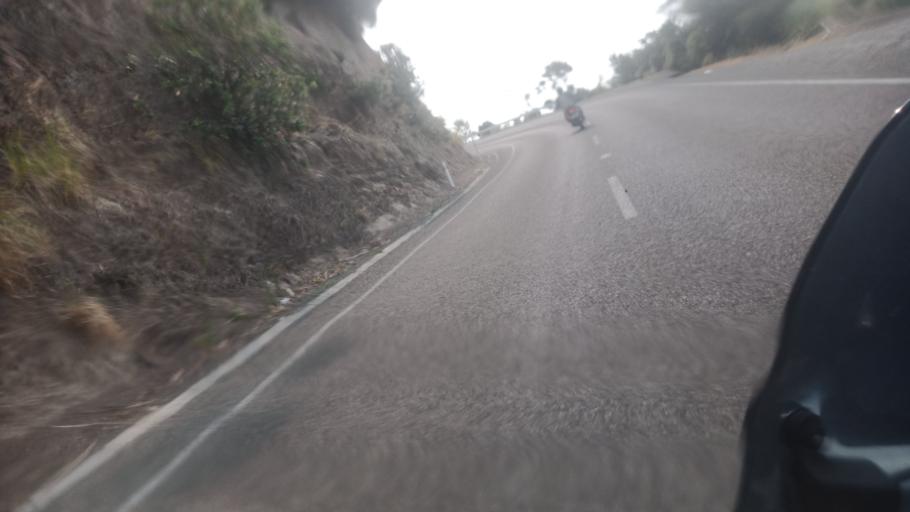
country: NZ
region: Bay of Plenty
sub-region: Opotiki District
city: Opotiki
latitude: -37.8784
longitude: 177.5778
